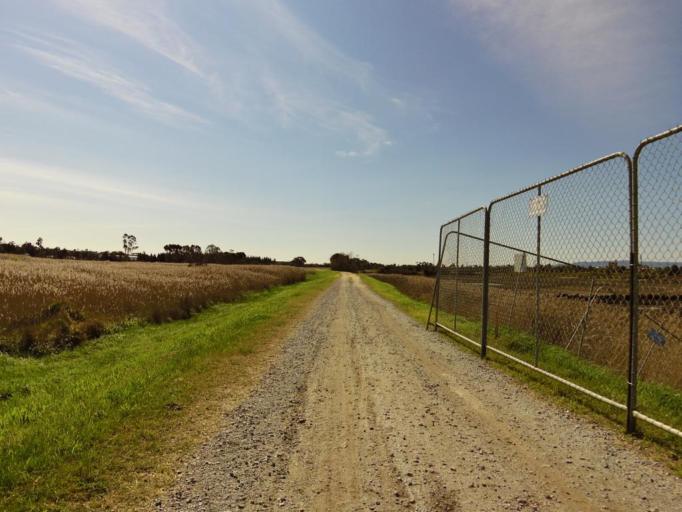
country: AU
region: Victoria
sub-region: Greater Dandenong
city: Keysborough
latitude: -38.0299
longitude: 145.1862
